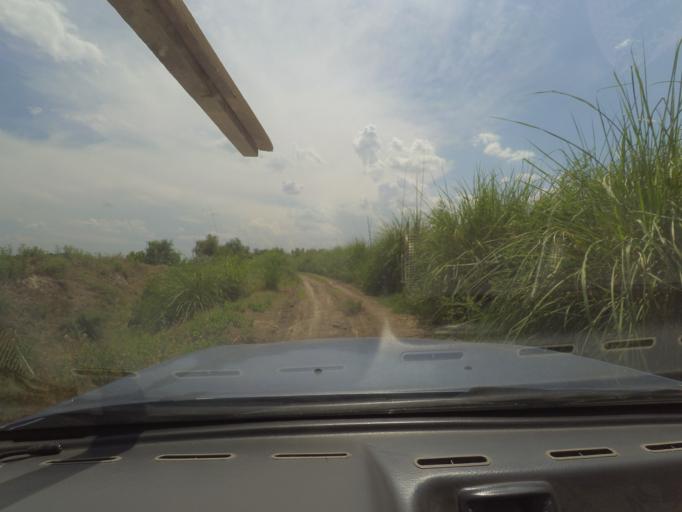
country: TJ
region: Viloyati Sughd
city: Buston
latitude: 40.5376
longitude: 69.0785
